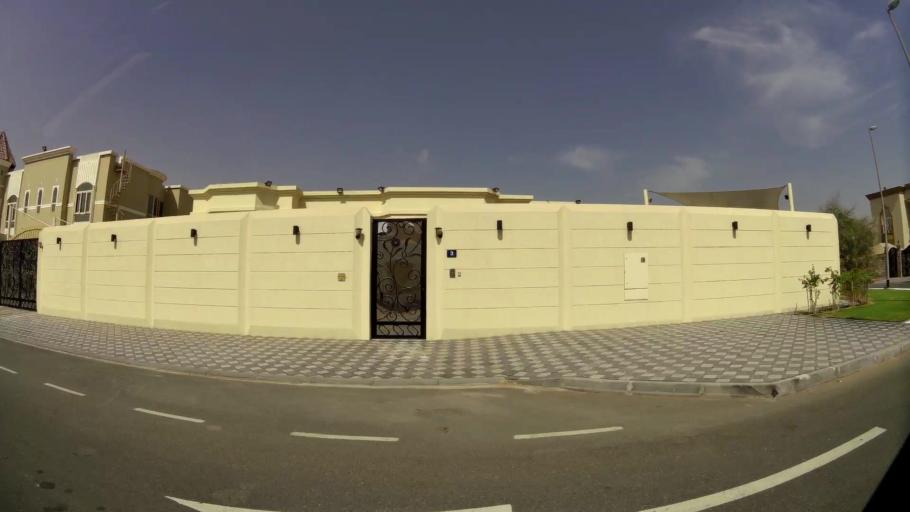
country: AE
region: Ash Shariqah
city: Sharjah
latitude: 25.2042
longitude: 55.4096
